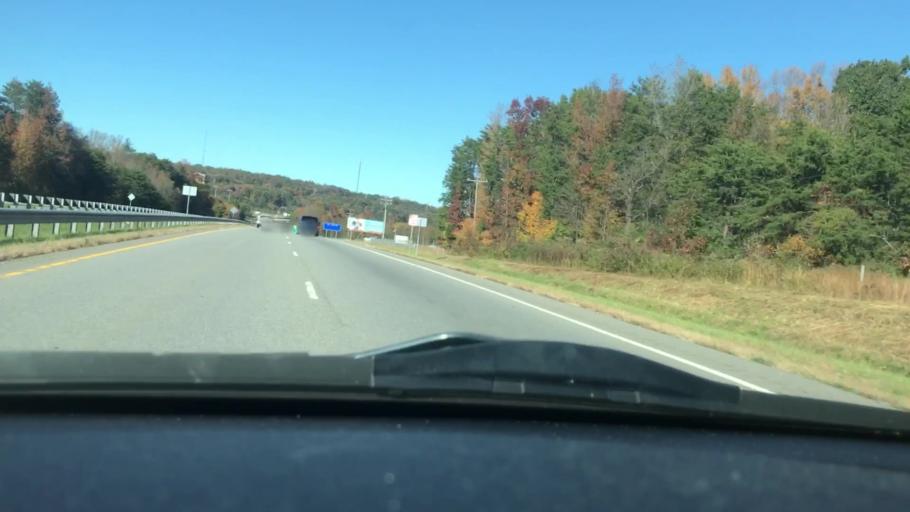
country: US
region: North Carolina
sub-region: Rockingham County
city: Mayodan
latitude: 36.4082
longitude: -79.9375
